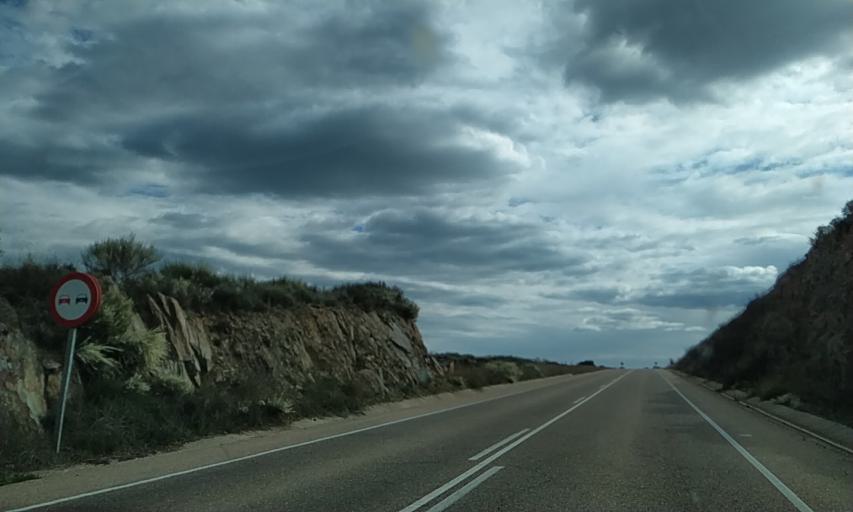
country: ES
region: Castille and Leon
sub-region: Provincia de Salamanca
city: Herguijuela de Ciudad Rodrigo
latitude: 40.4902
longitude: -6.5811
